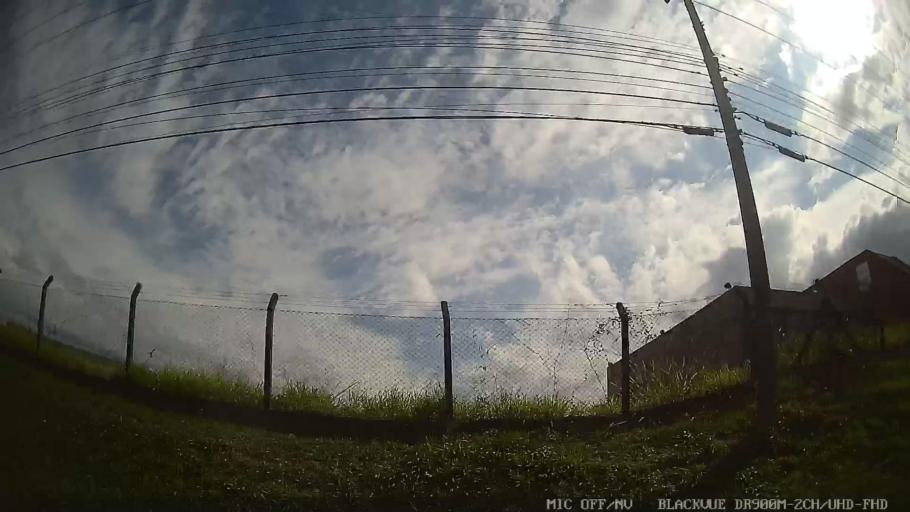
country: BR
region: Sao Paulo
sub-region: Salto
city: Salto
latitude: -23.1454
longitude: -47.2511
